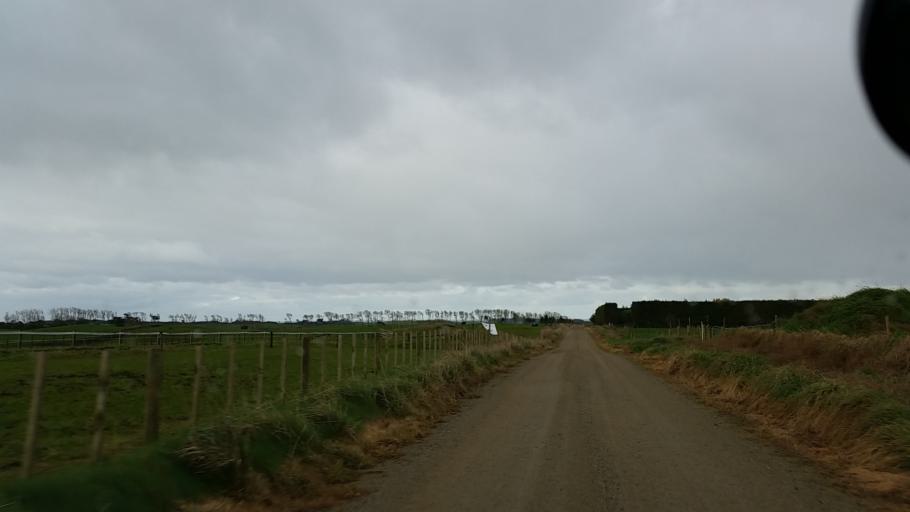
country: NZ
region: Taranaki
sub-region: South Taranaki District
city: Patea
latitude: -39.7640
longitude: 174.6424
